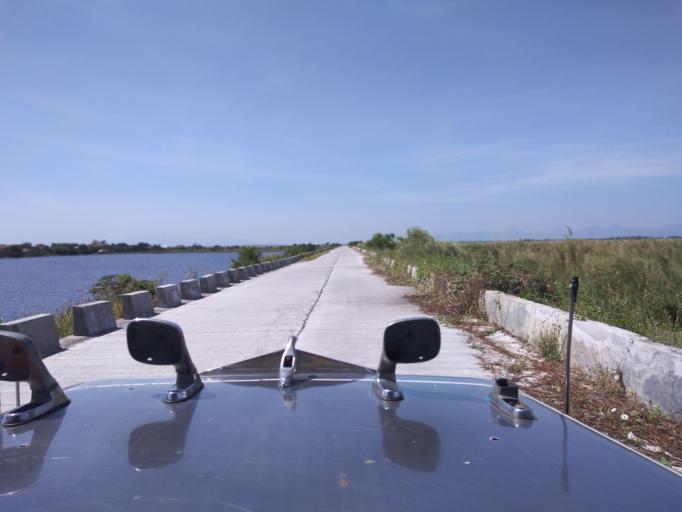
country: PH
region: Central Luzon
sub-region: Province of Pampanga
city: Minalin
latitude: 14.9841
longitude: 120.6924
